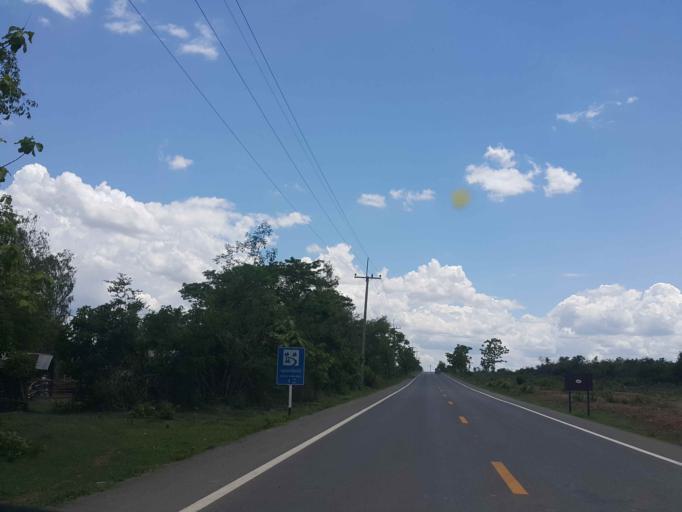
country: TH
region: Phrae
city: Nong Muang Khai
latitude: 18.1972
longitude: 100.2218
